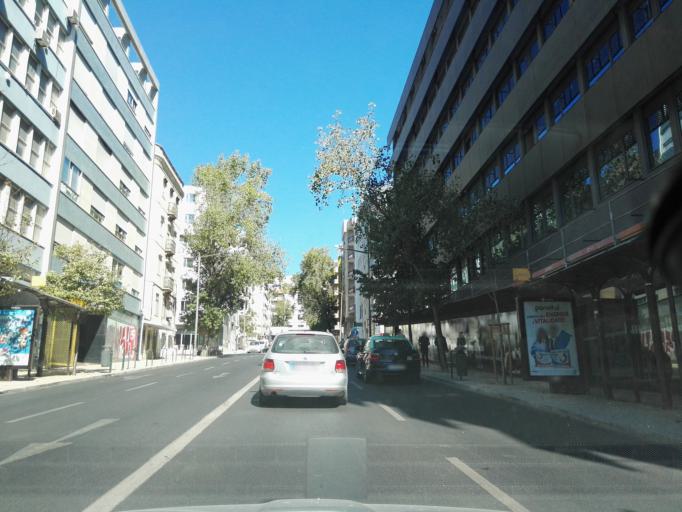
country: PT
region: Lisbon
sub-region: Lisbon
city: Lisbon
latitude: 38.7265
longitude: -9.1451
